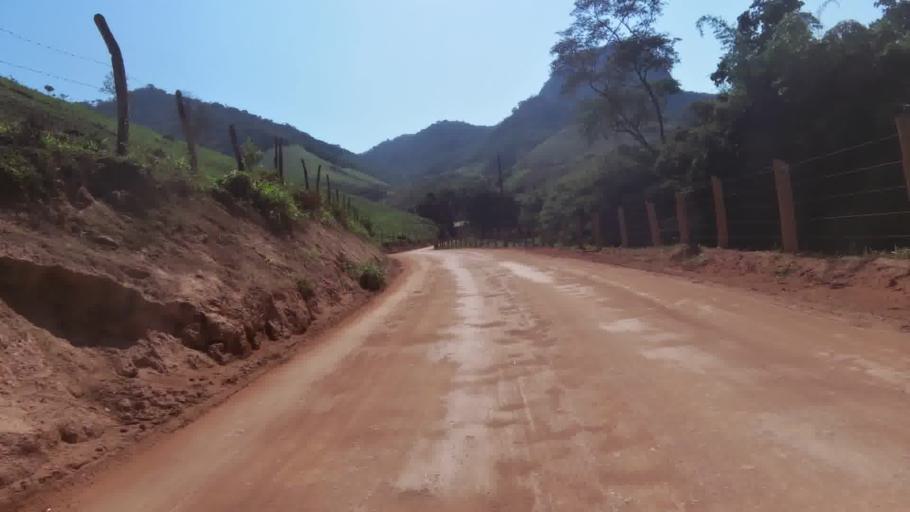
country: BR
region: Espirito Santo
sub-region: Alfredo Chaves
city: Alfredo Chaves
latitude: -20.6331
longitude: -40.7650
